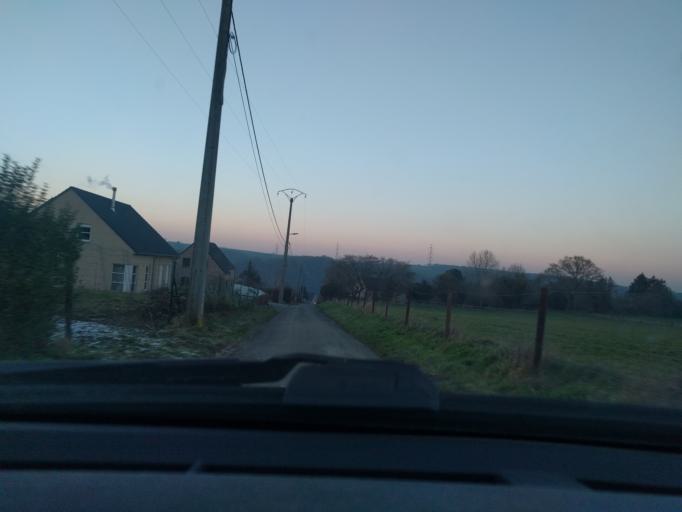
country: BE
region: Wallonia
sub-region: Province de Namur
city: Andenne
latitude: 50.4854
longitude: 5.0346
